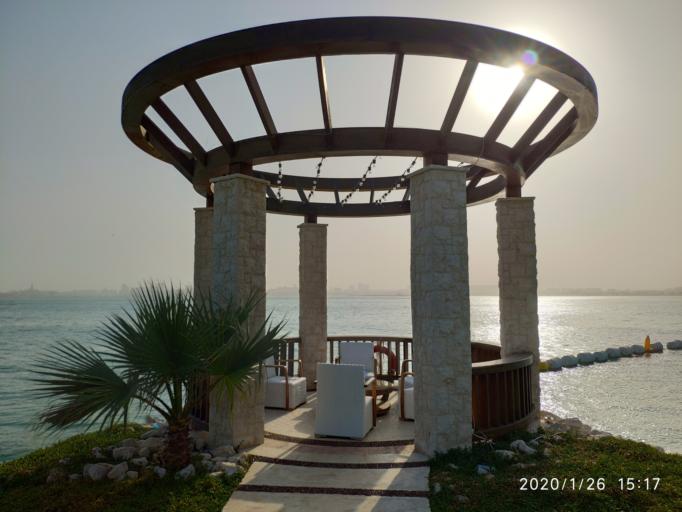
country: QA
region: Baladiyat ad Dawhah
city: Doha
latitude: 25.3172
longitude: 51.5388
